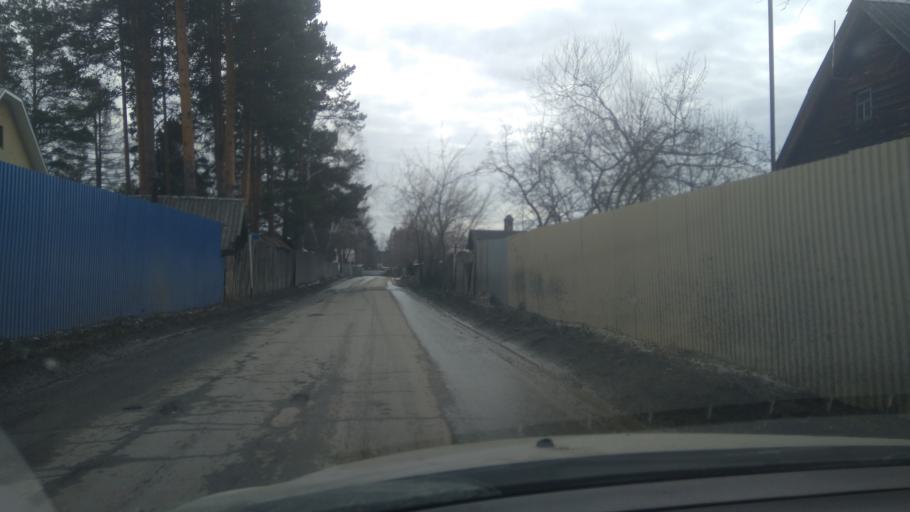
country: RU
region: Sverdlovsk
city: Severka
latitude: 56.8500
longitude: 60.3848
